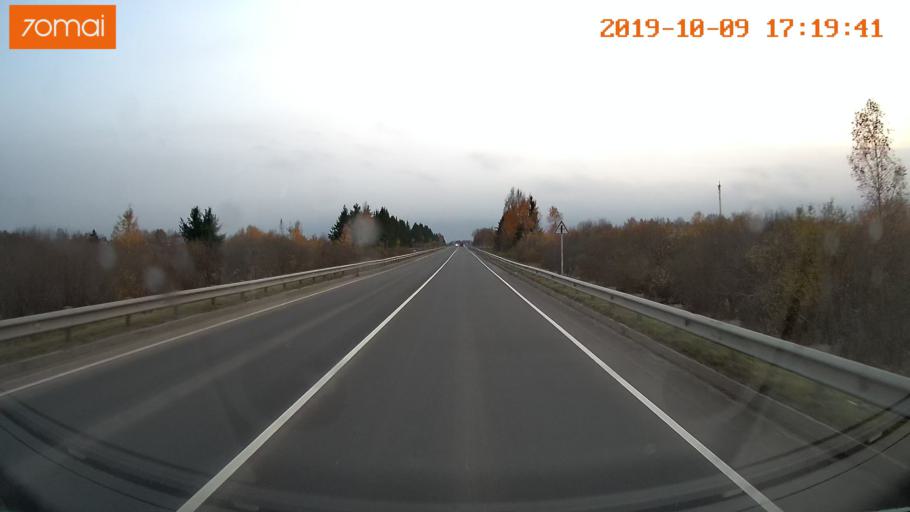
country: RU
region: Ivanovo
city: Furmanov
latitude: 57.2431
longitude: 41.1499
